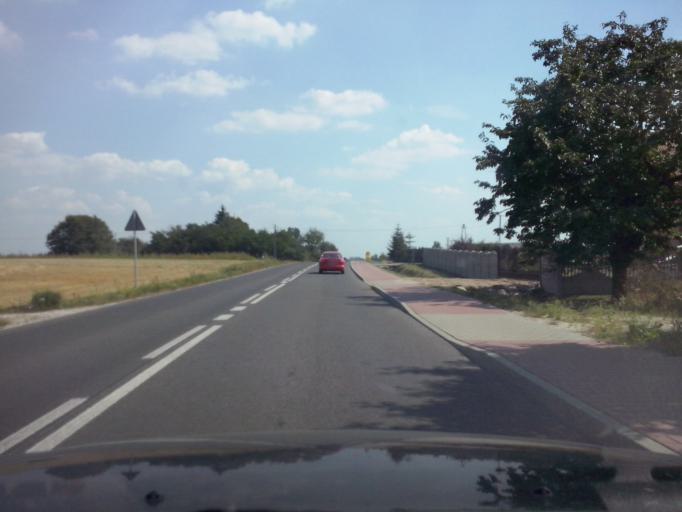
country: PL
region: Swietokrzyskie
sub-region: Powiat buski
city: Gnojno
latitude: 50.5872
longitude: 20.9107
